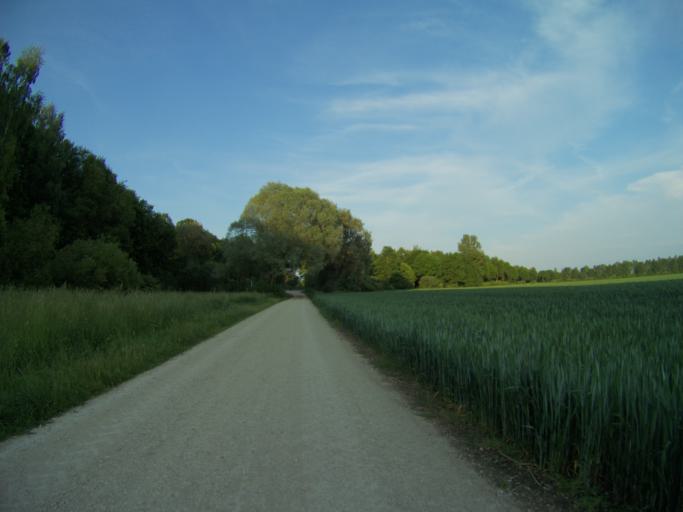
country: DE
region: Bavaria
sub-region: Upper Bavaria
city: Marzling
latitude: 48.3713
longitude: 11.7869
